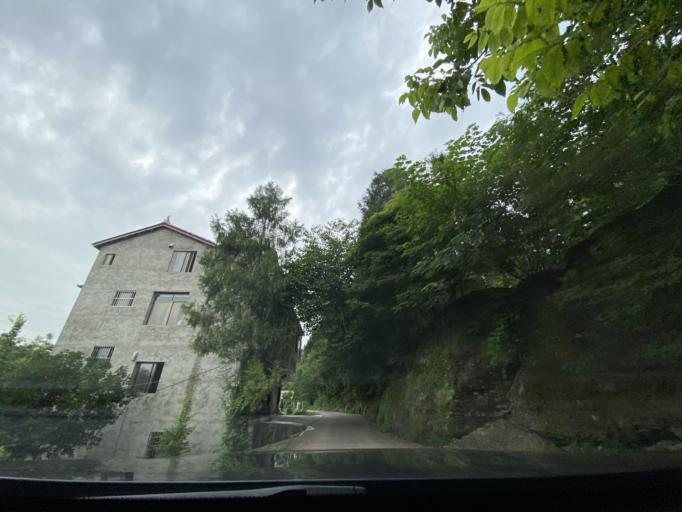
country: CN
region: Sichuan
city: Jiancheng
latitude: 30.3871
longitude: 104.4873
